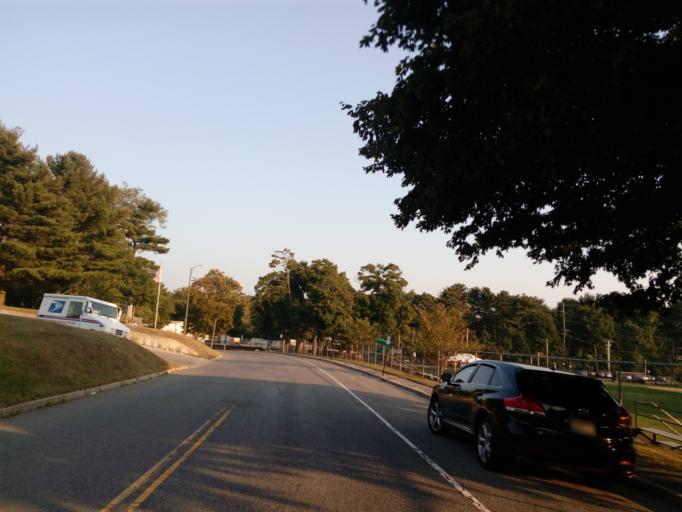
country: US
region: New York
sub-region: Nassau County
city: Locust Valley
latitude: 40.8751
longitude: -73.6002
